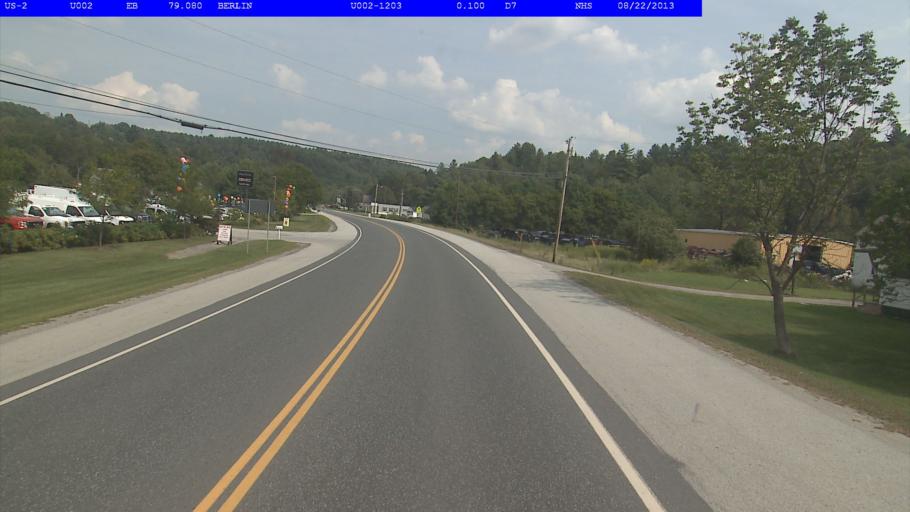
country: US
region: Vermont
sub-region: Washington County
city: Montpelier
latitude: 44.2413
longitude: -72.5411
